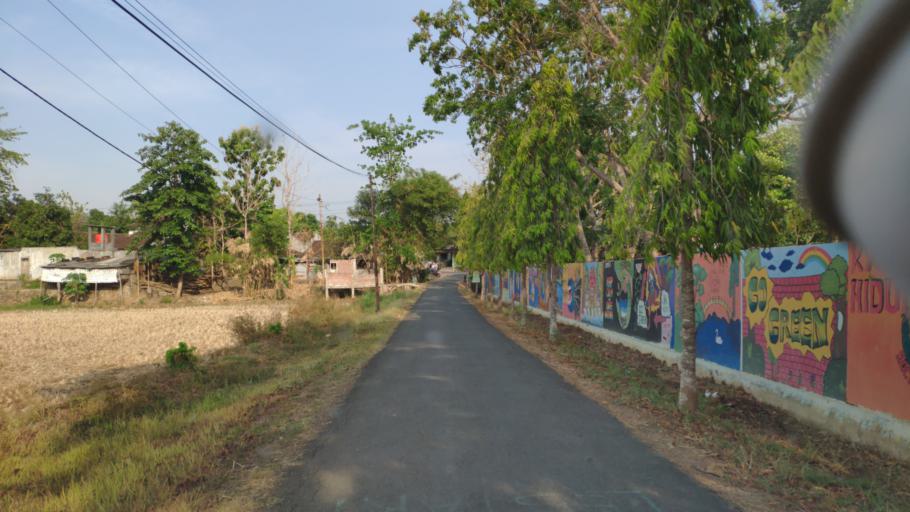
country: ID
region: Central Java
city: Wonosari
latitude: -6.9465
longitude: 111.4303
